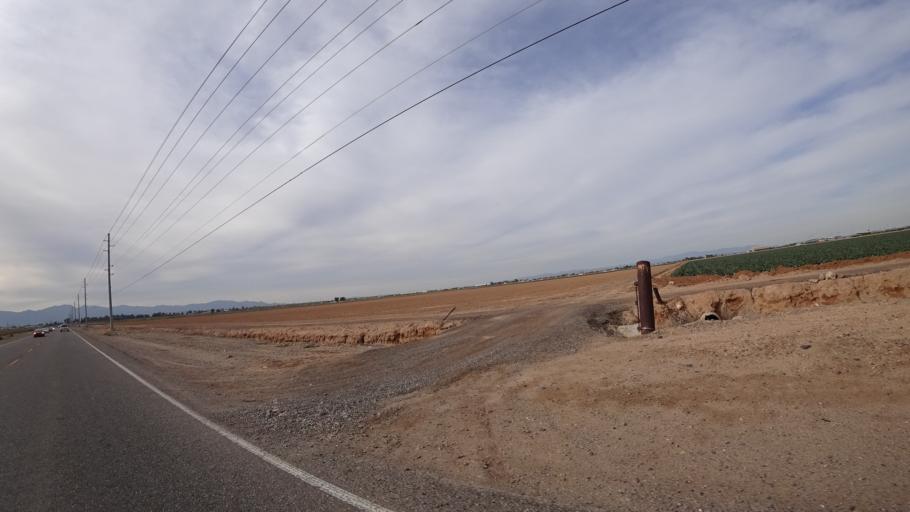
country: US
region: Arizona
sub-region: Maricopa County
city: Youngtown
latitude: 33.5653
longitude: -112.3298
